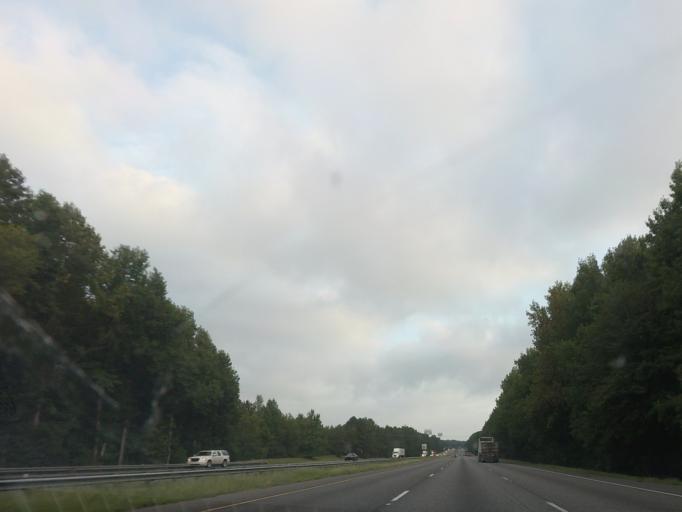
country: US
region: Georgia
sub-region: Butts County
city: Jackson
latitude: 33.2193
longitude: -84.0700
